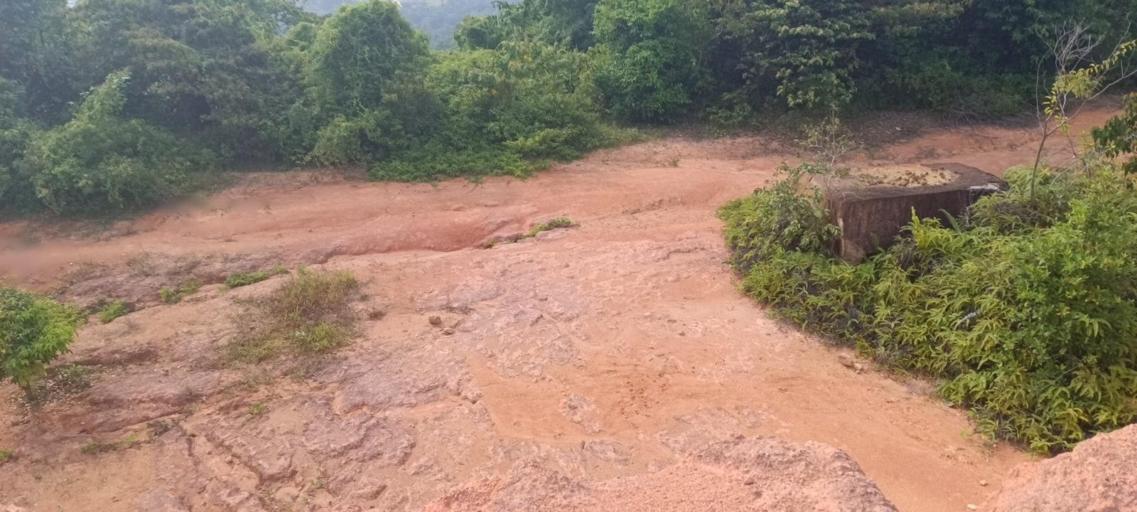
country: MY
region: Penang
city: Juru
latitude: 5.2742
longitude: 100.4207
